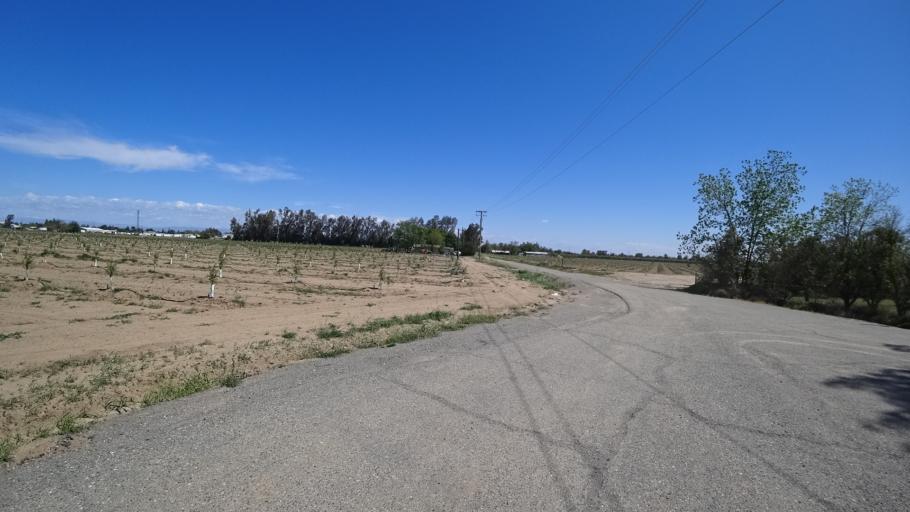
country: US
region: California
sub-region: Glenn County
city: Orland
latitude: 39.7332
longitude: -122.2053
